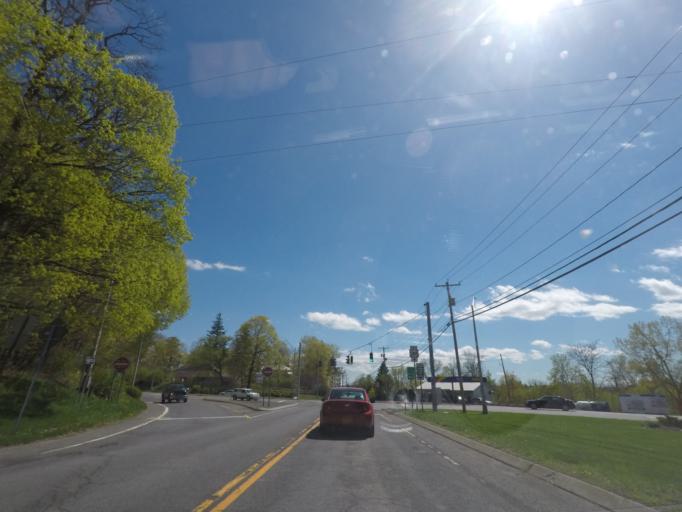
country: US
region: New York
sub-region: Greene County
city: Catskill
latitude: 42.2274
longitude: -73.8620
